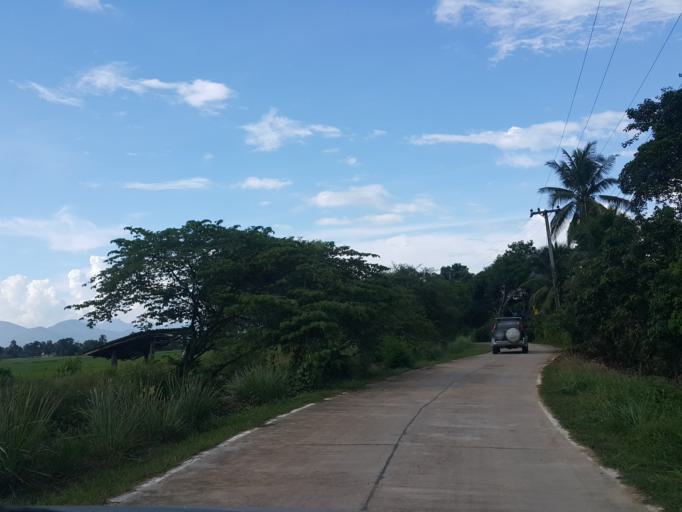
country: TH
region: Chiang Mai
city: Phrao
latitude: 19.3384
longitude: 99.1846
